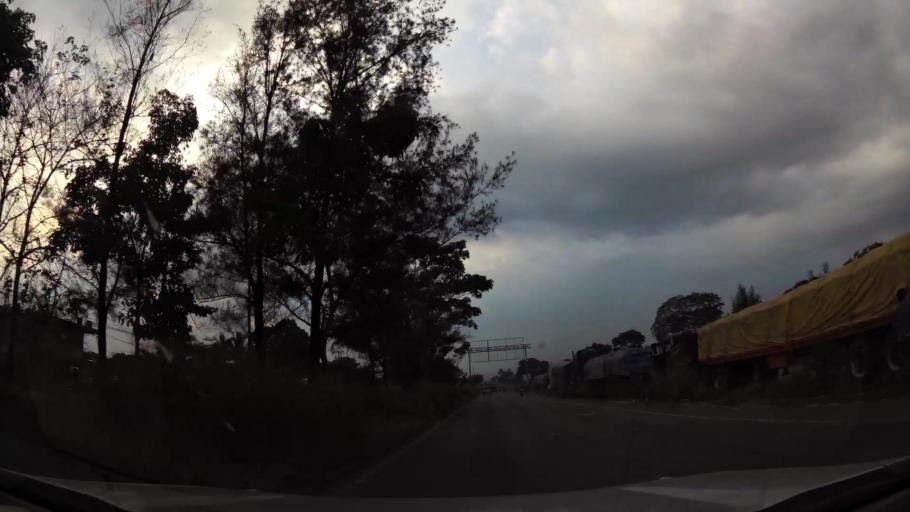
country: GT
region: Escuintla
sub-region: Municipio de Escuintla
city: Escuintla
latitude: 14.2813
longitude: -90.7844
